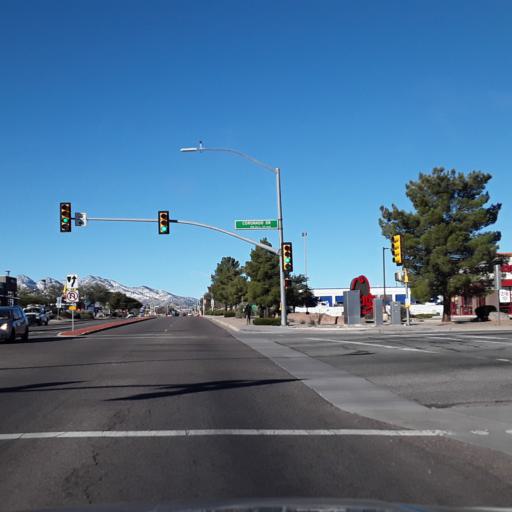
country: US
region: Arizona
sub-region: Cochise County
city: Sierra Vista
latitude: 31.5547
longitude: -110.2773
